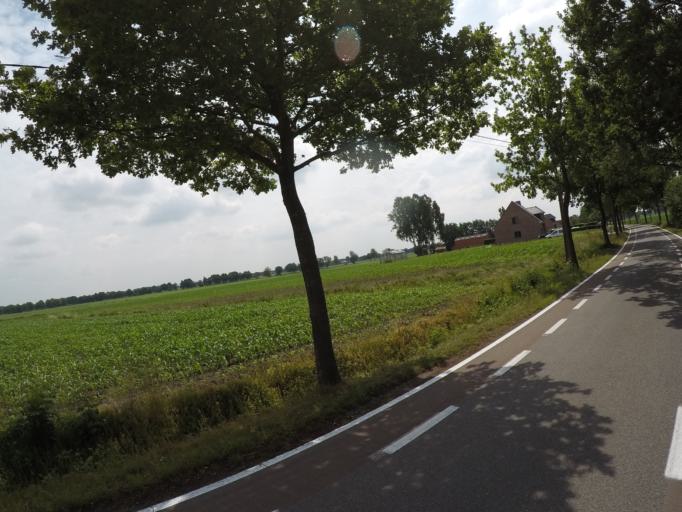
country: BE
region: Flanders
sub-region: Provincie Antwerpen
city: Kalmthout
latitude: 51.4222
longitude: 4.5039
